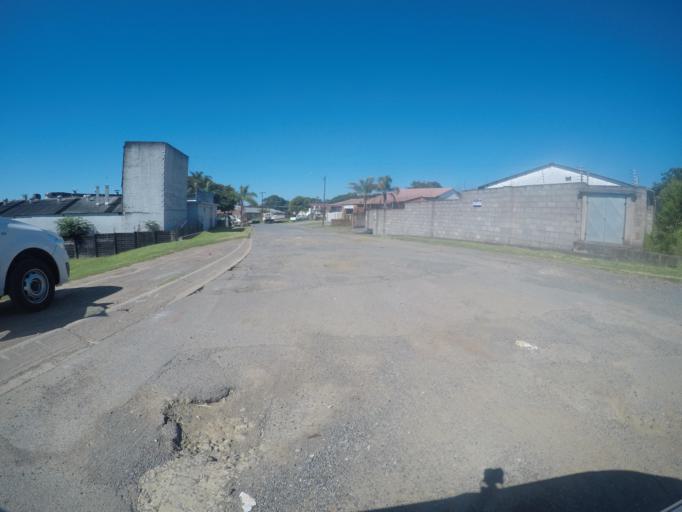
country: ZA
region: Eastern Cape
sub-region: Buffalo City Metropolitan Municipality
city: East London
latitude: -32.9391
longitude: 28.0022
